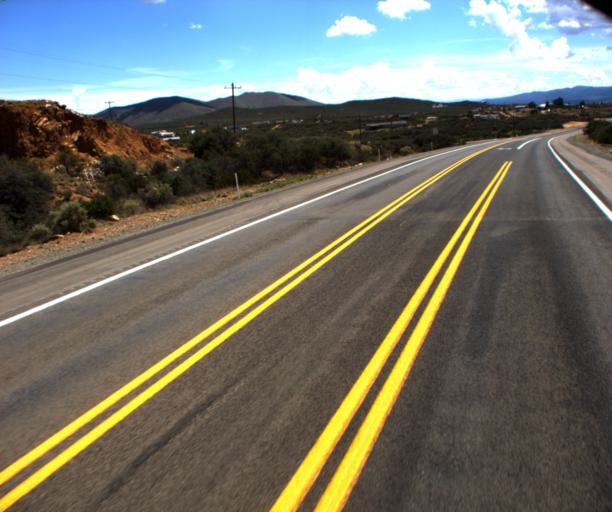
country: US
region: Arizona
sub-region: Yavapai County
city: Dewey-Humboldt
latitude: 34.5474
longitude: -112.1640
